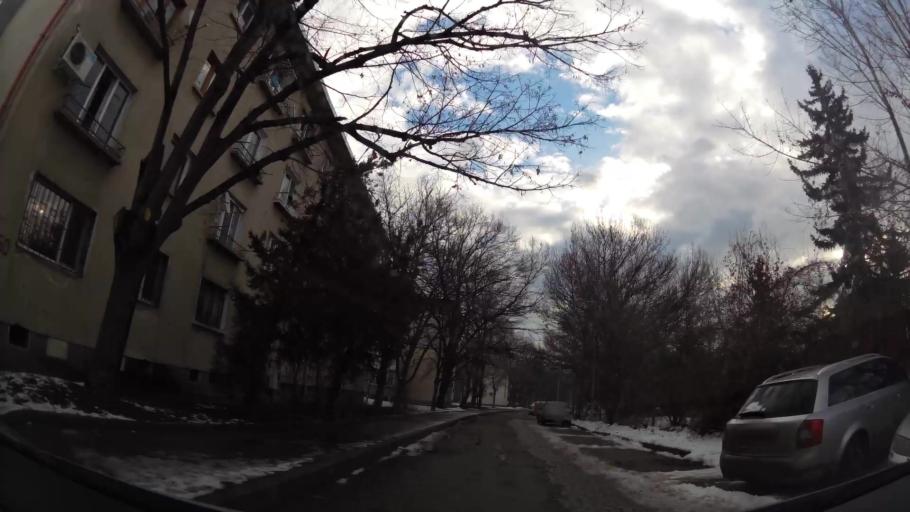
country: BG
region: Sofia-Capital
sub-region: Stolichna Obshtina
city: Sofia
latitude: 42.7044
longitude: 23.2797
